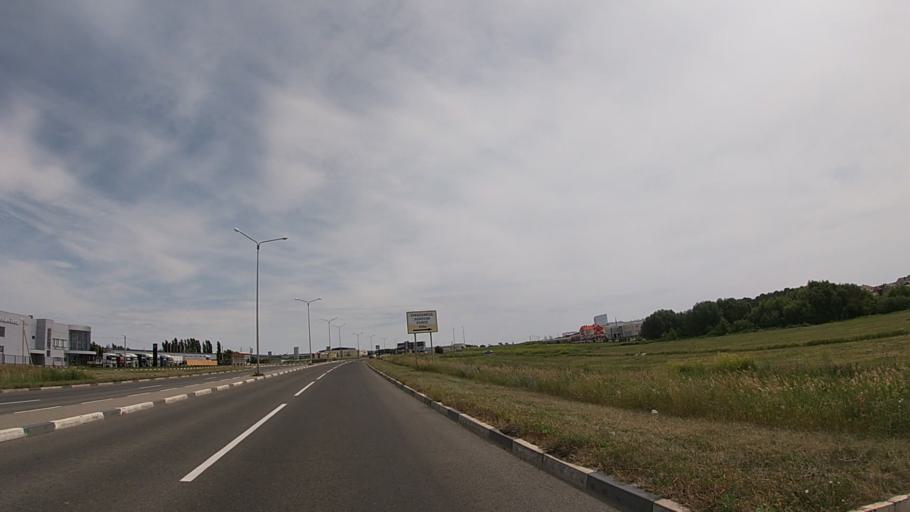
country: RU
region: Belgorod
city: Severnyy
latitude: 50.6581
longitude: 36.5486
